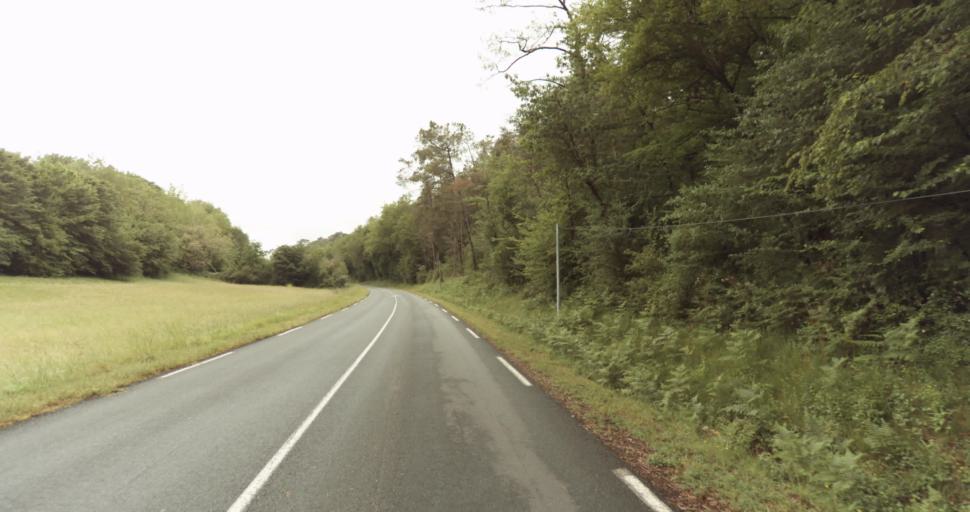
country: FR
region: Aquitaine
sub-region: Departement de la Dordogne
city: Belves
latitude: 44.6658
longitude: 1.0136
